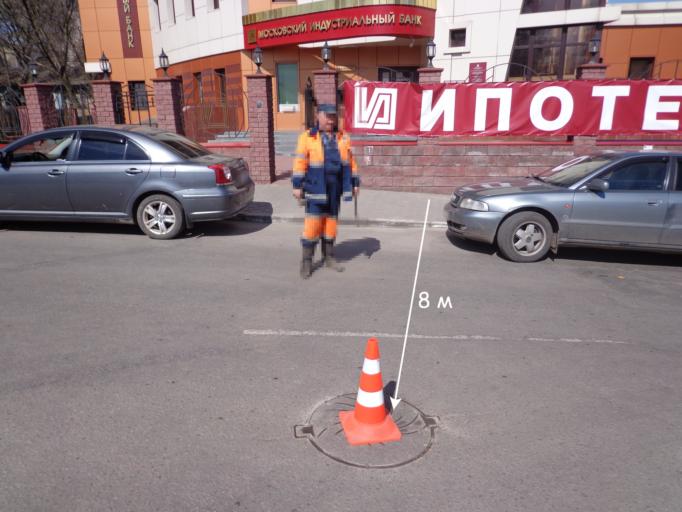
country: RU
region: Voronezj
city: Voronezh
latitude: 51.6664
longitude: 39.2111
